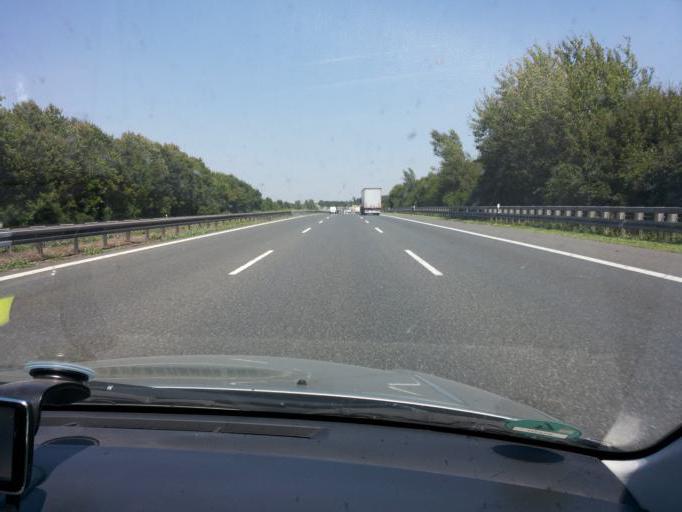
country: DE
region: Bavaria
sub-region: Upper Bavaria
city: Stammham
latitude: 48.8657
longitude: 11.4669
